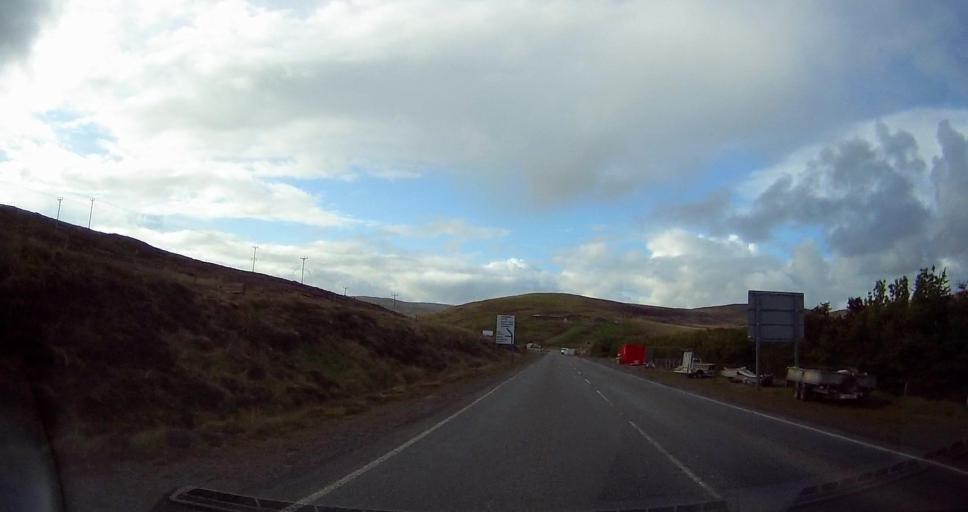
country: GB
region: Scotland
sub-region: Shetland Islands
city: Lerwick
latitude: 60.3456
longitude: -1.2529
